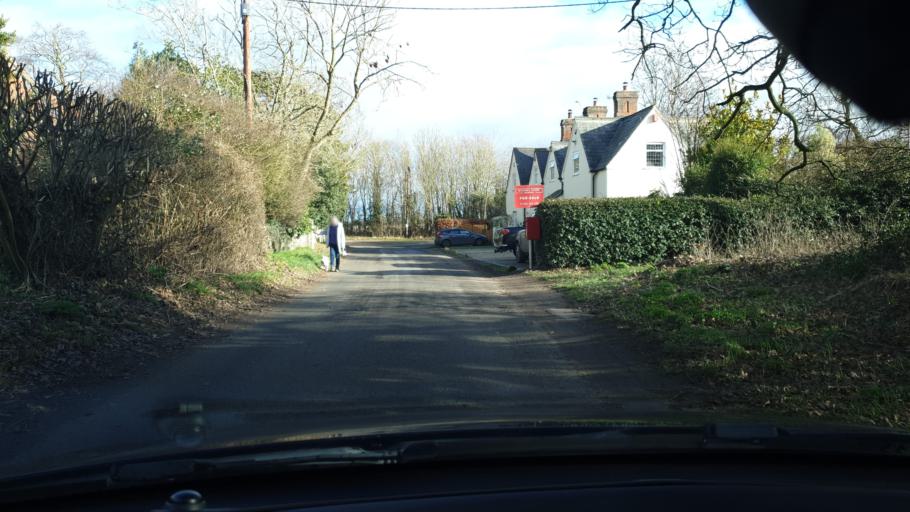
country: GB
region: England
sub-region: Essex
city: Alresford
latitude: 51.8607
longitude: 1.0218
